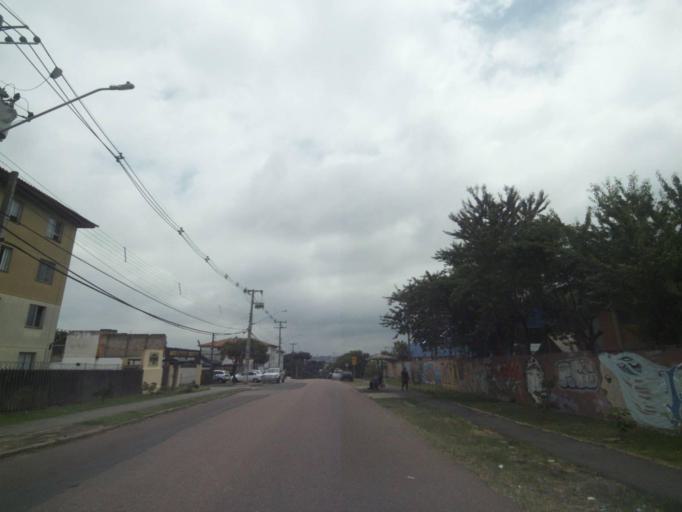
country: BR
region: Parana
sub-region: Curitiba
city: Curitiba
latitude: -25.4941
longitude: -49.3499
